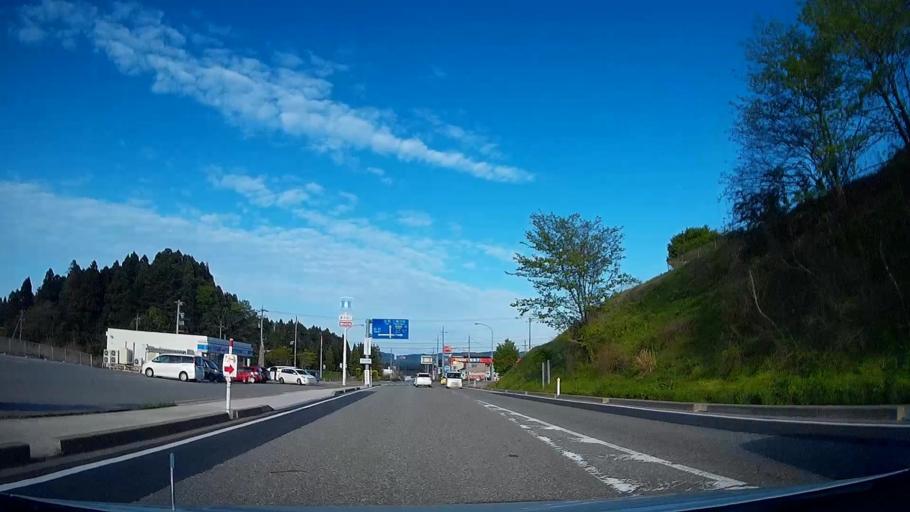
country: JP
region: Ishikawa
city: Nanao
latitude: 37.0466
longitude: 136.9469
